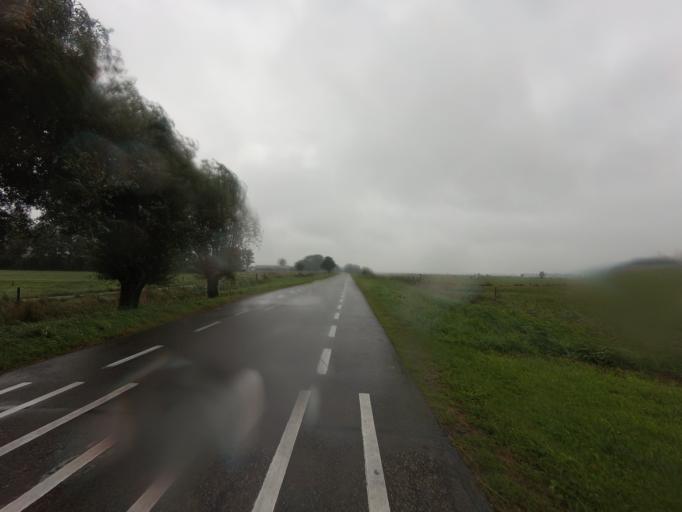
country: NL
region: Friesland
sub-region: Gemeente Smallingerland
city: Oudega
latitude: 53.0967
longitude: 5.9590
